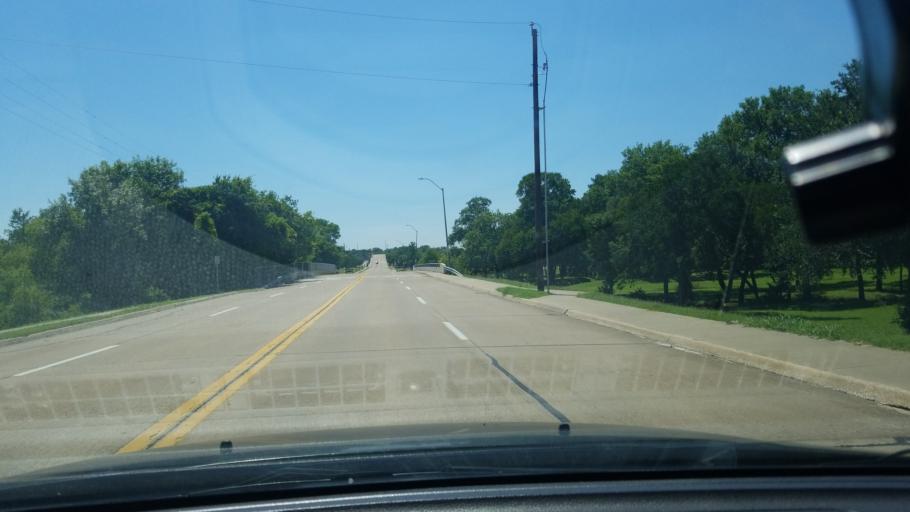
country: US
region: Texas
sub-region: Dallas County
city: Mesquite
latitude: 32.7560
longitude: -96.6082
